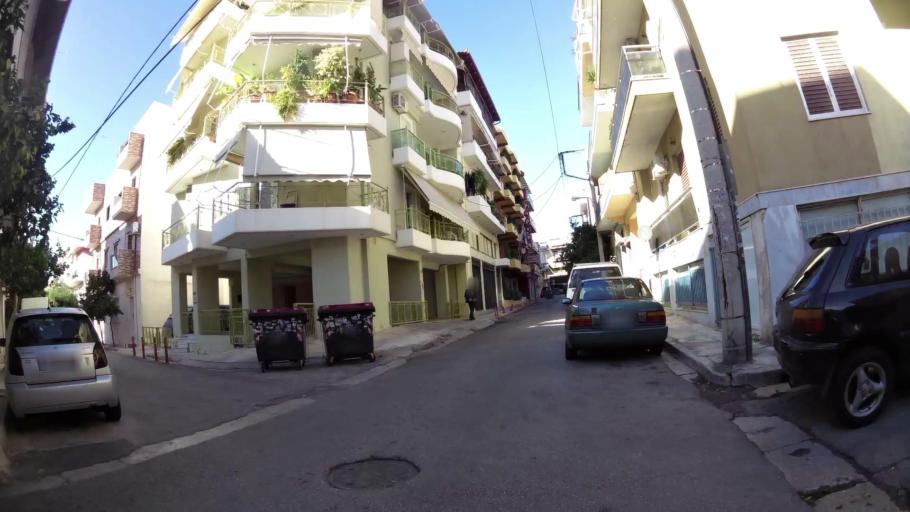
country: GR
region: Attica
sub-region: Nomos Piraios
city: Nikaia
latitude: 37.9677
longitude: 23.6520
